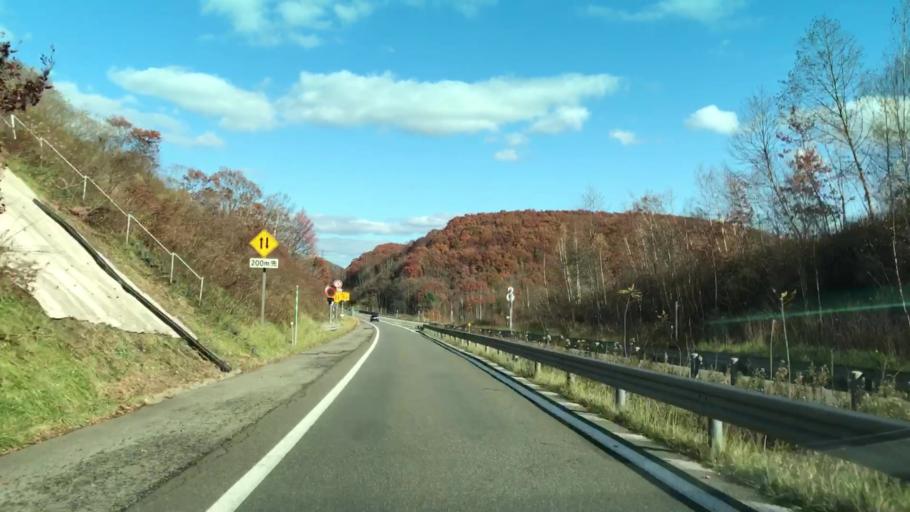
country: JP
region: Hokkaido
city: Chitose
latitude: 42.8805
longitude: 141.7540
